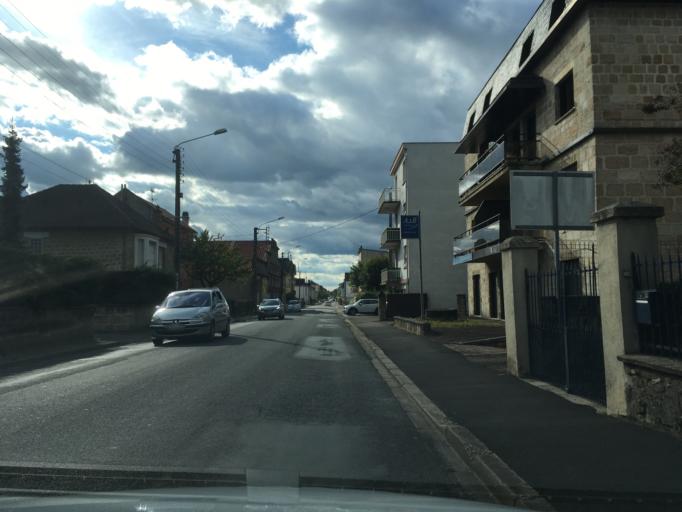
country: FR
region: Limousin
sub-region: Departement de la Correze
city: Malemort-sur-Correze
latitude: 45.1579
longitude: 1.5525
